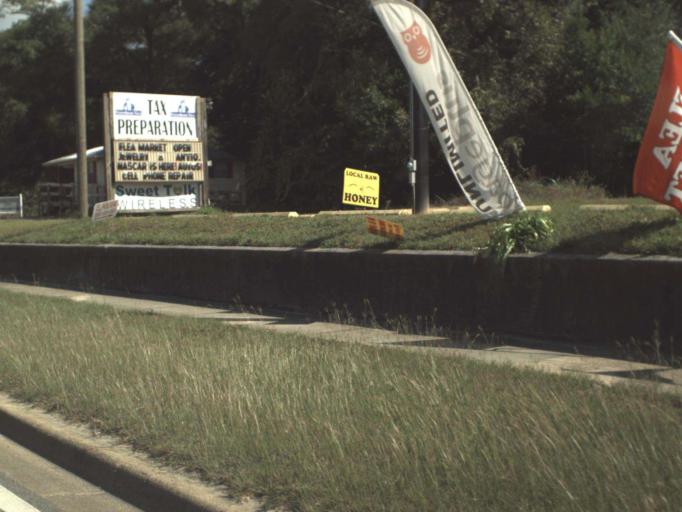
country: US
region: Florida
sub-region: Walton County
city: DeFuniak Springs
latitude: 30.7135
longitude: -86.1227
